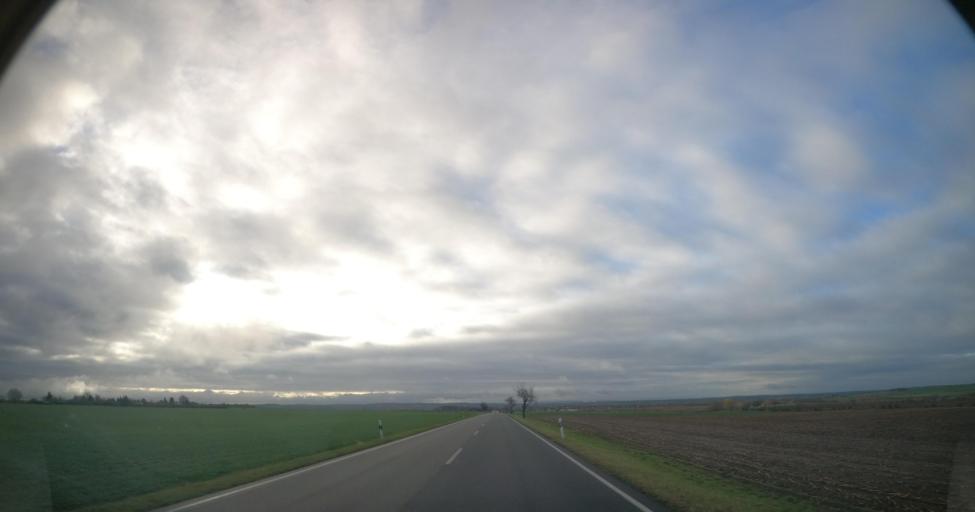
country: DE
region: Brandenburg
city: Gartz
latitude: 53.2285
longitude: 14.3965
